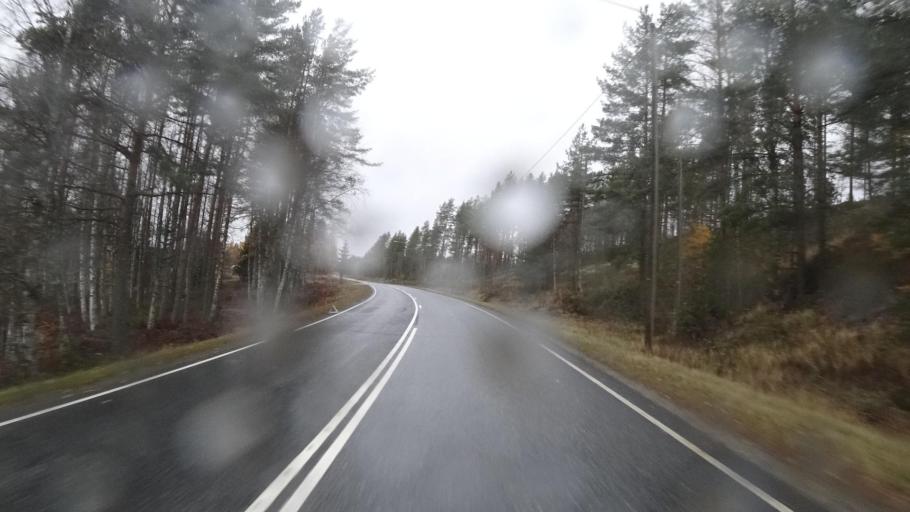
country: FI
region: Northern Savo
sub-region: Koillis-Savo
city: Tuusniemi
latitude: 62.8723
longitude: 28.3302
